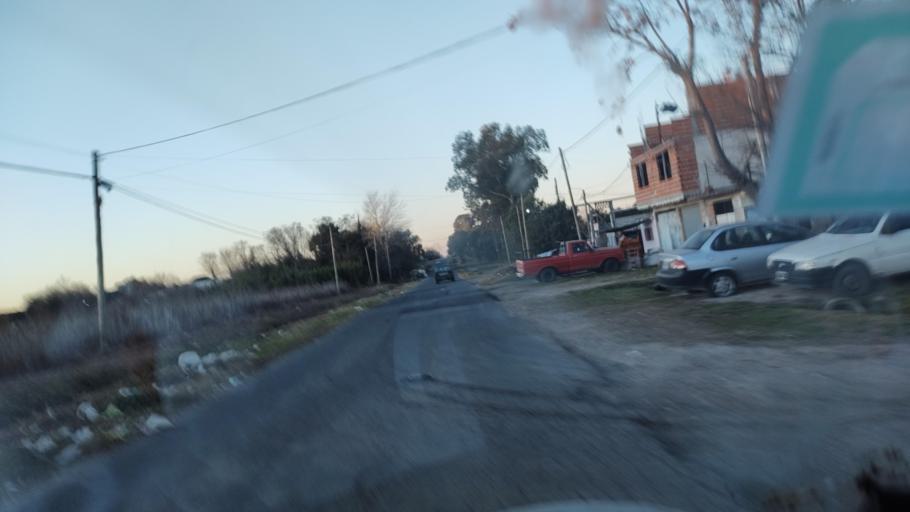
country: AR
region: Buenos Aires
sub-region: Partido de La Plata
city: La Plata
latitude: -34.9102
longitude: -58.0163
